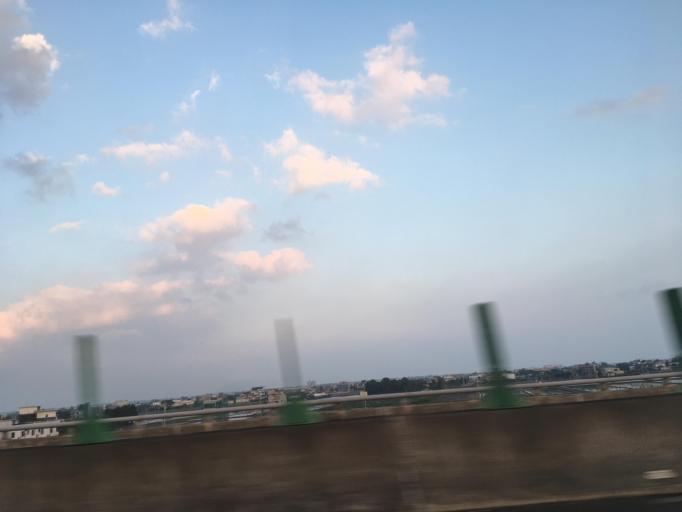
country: TW
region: Taiwan
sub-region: Yilan
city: Yilan
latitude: 24.8130
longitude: 121.7809
